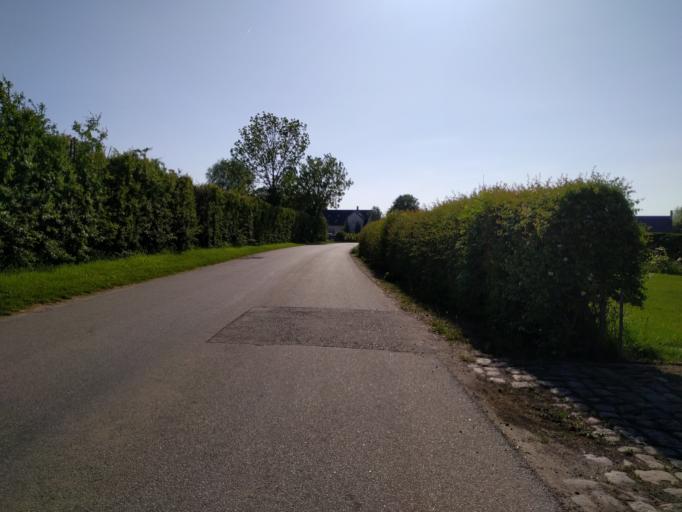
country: DK
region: South Denmark
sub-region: Kerteminde Kommune
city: Munkebo
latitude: 55.4348
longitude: 10.5925
